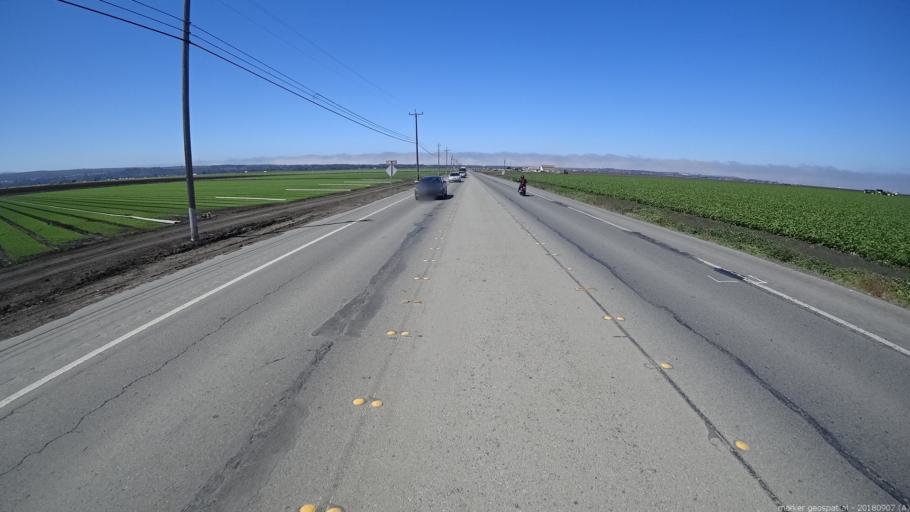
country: US
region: California
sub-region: Monterey County
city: Boronda
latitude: 36.6787
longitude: -121.7090
